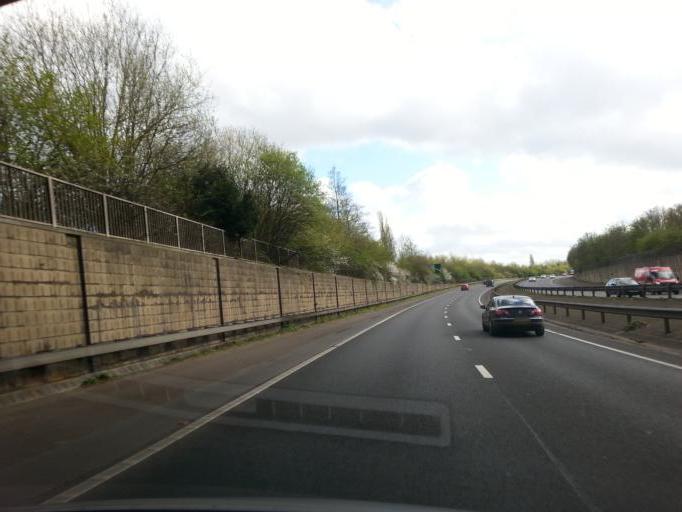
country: GB
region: England
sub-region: Surrey
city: Seale
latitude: 51.2550
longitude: -0.7298
